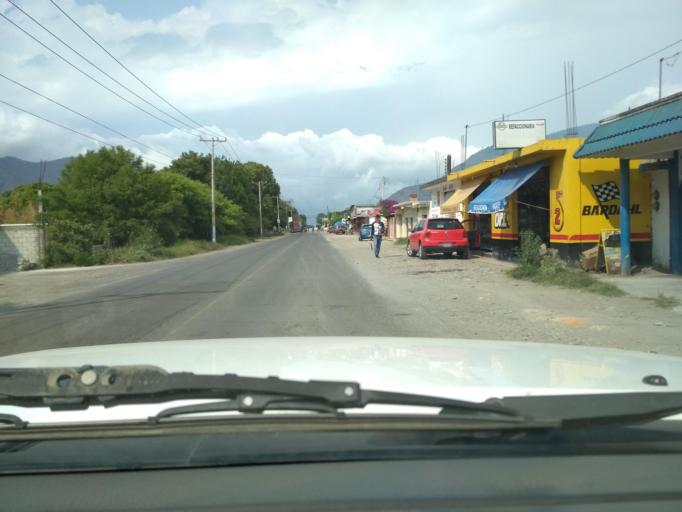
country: MX
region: Veracruz
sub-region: Acultzingo
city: Acatla
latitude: 18.7614
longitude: -97.2274
